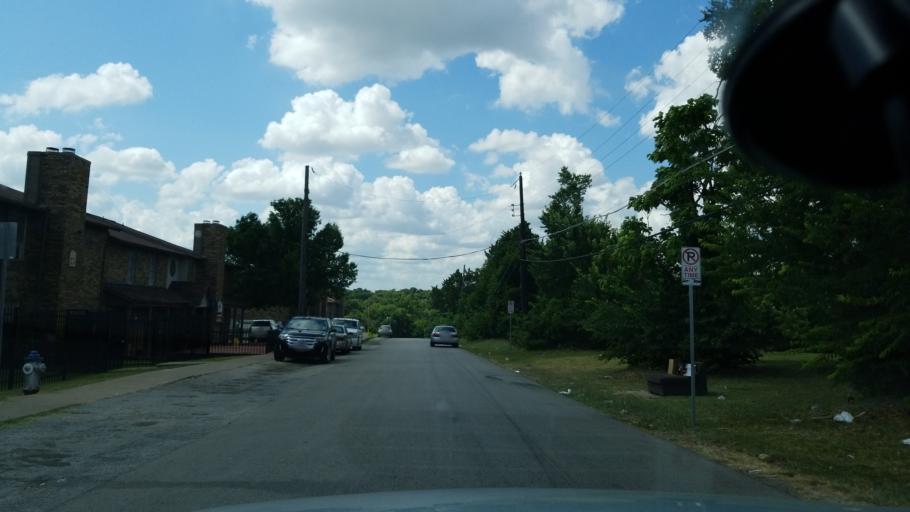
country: US
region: Texas
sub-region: Dallas County
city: Cockrell Hill
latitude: 32.6976
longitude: -96.8372
